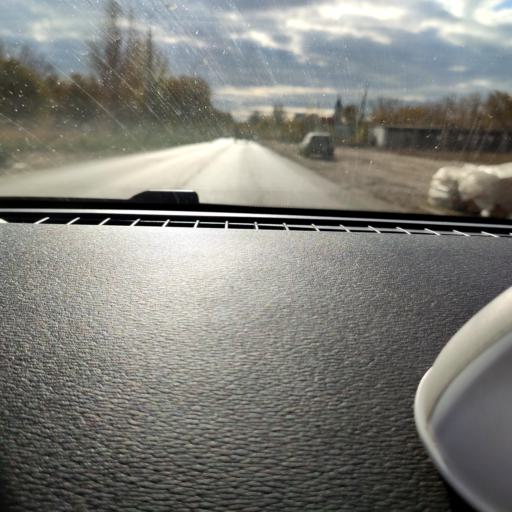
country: RU
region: Samara
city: Petra-Dubrava
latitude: 53.2456
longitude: 50.3087
